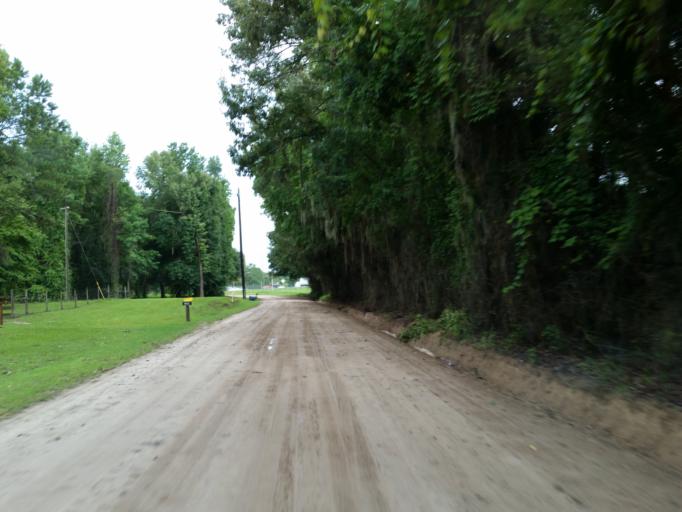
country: US
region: Florida
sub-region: Alachua County
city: High Springs
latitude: 29.9812
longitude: -82.5792
